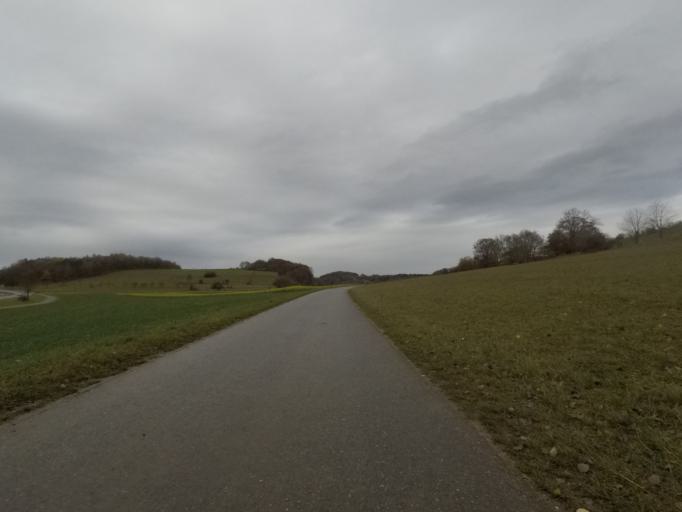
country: DE
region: Baden-Wuerttemberg
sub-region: Tuebingen Region
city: Sankt Johann
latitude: 48.4182
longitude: 9.2865
